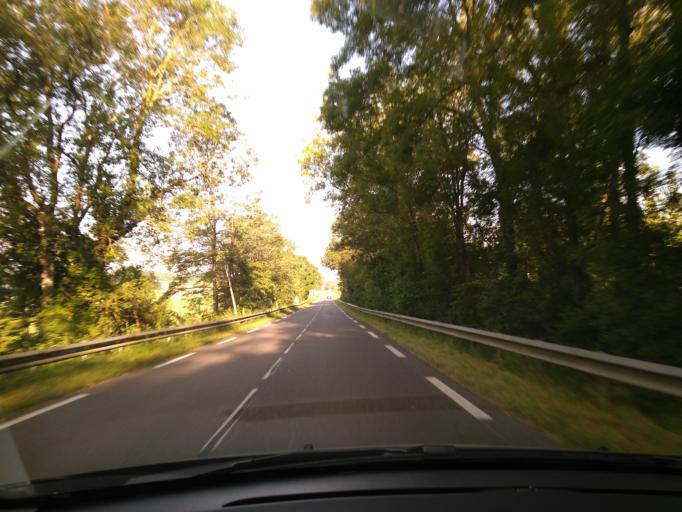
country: FR
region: Midi-Pyrenees
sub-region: Departement du Gers
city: Gondrin
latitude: 43.8782
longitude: 0.2141
